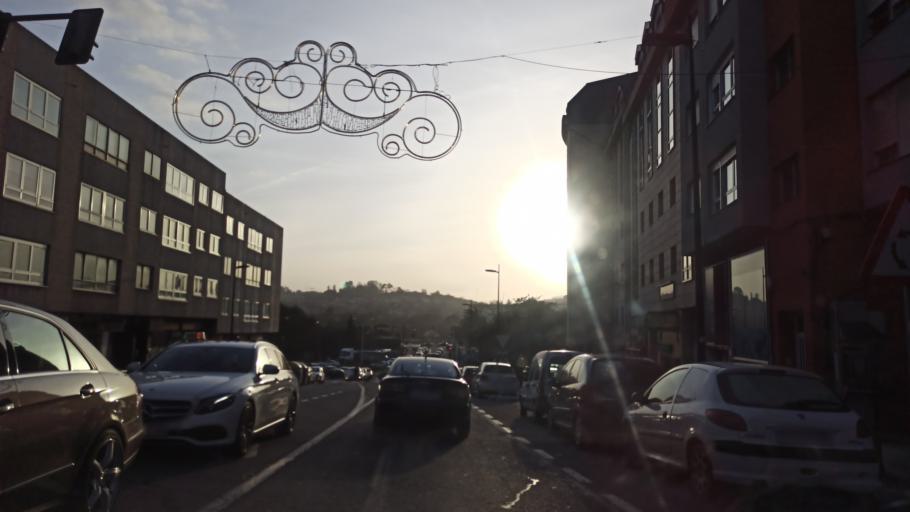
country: ES
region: Galicia
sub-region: Provincia da Coruna
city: Cambre
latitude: 43.3177
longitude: -8.3569
